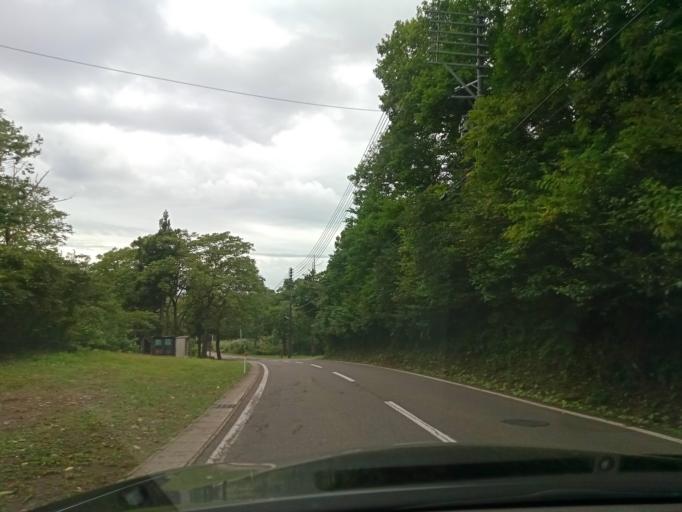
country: JP
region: Niigata
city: Arai
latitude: 36.8825
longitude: 138.1802
